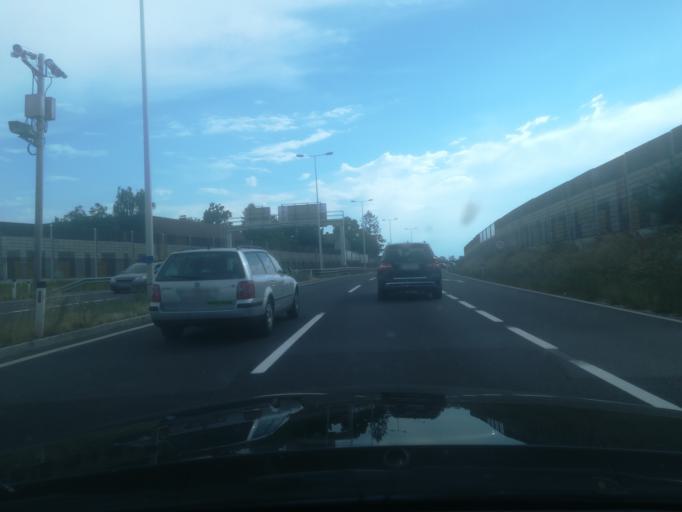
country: AT
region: Upper Austria
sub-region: Politischer Bezirk Linz-Land
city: Horsching
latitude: 48.2184
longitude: 14.1899
